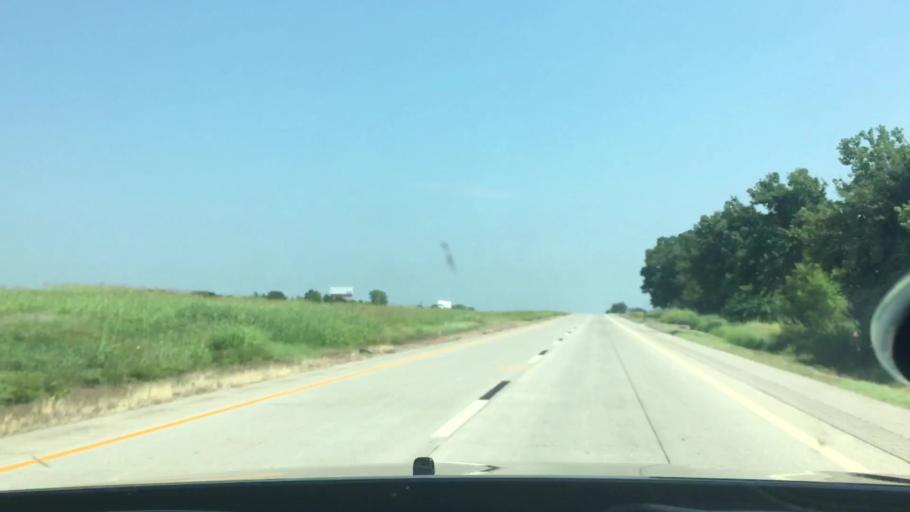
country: US
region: Oklahoma
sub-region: Atoka County
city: Atoka
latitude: 34.1919
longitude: -96.2421
